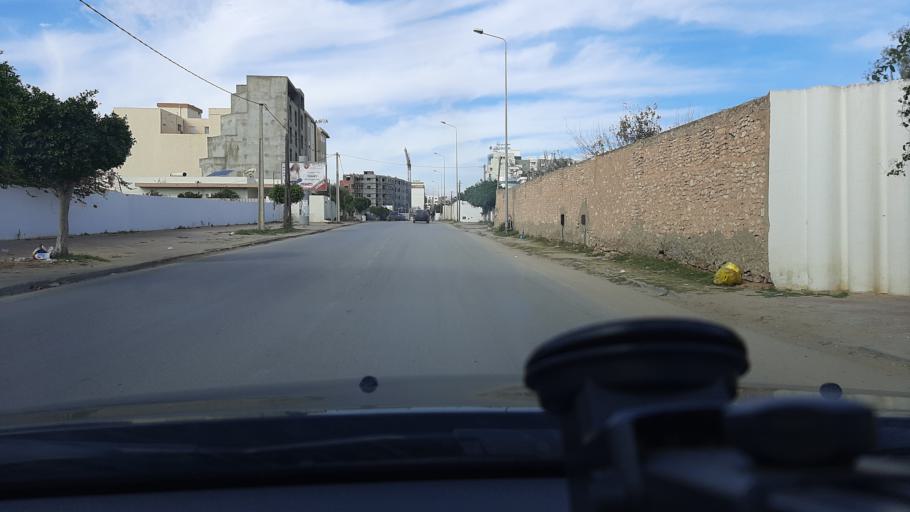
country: TN
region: Safaqis
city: Sfax
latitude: 34.7603
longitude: 10.7313
